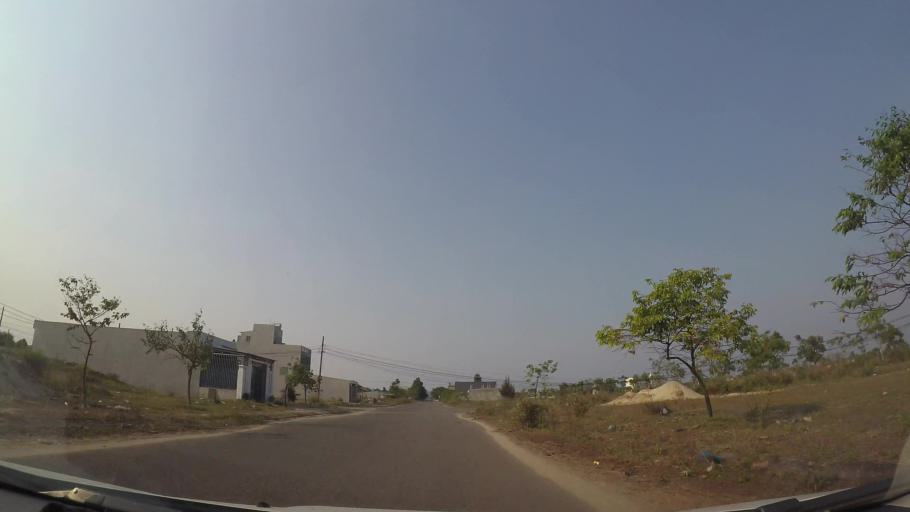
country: VN
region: Da Nang
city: Ngu Hanh Son
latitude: 15.9585
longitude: 108.2568
